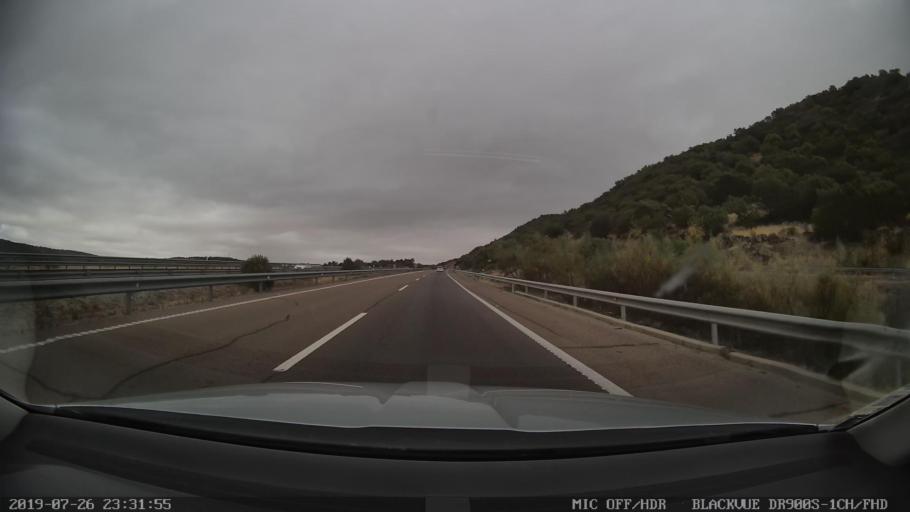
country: ES
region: Extremadura
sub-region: Provincia de Caceres
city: Puerto de Santa Cruz
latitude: 39.3084
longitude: -5.8572
